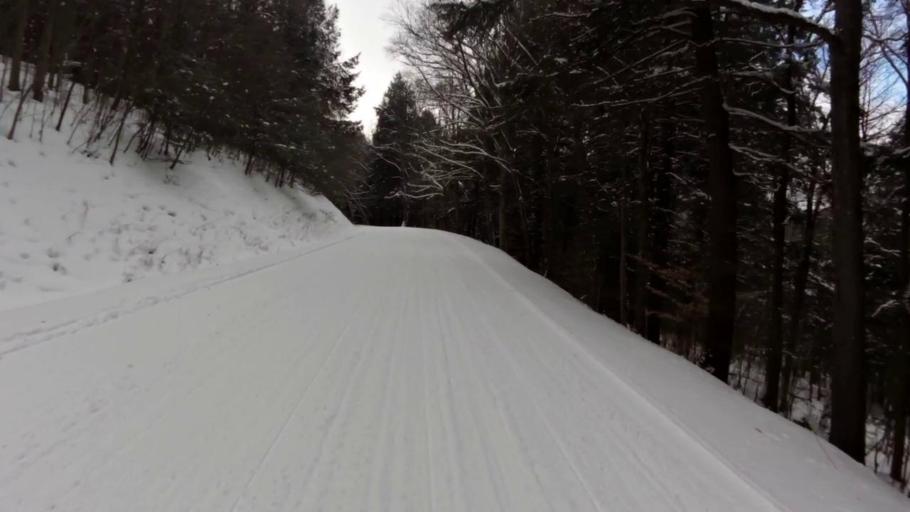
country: US
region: New York
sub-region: Cattaraugus County
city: Salamanca
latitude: 42.0638
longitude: -78.7637
